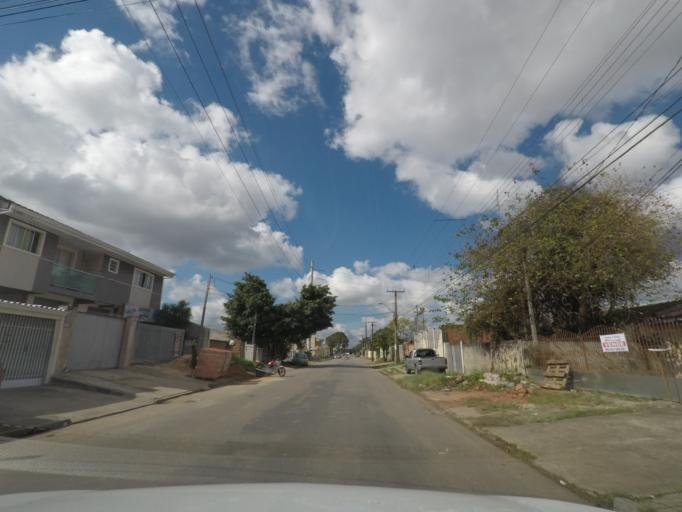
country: BR
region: Parana
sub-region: Sao Jose Dos Pinhais
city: Sao Jose dos Pinhais
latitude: -25.4882
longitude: -49.2305
